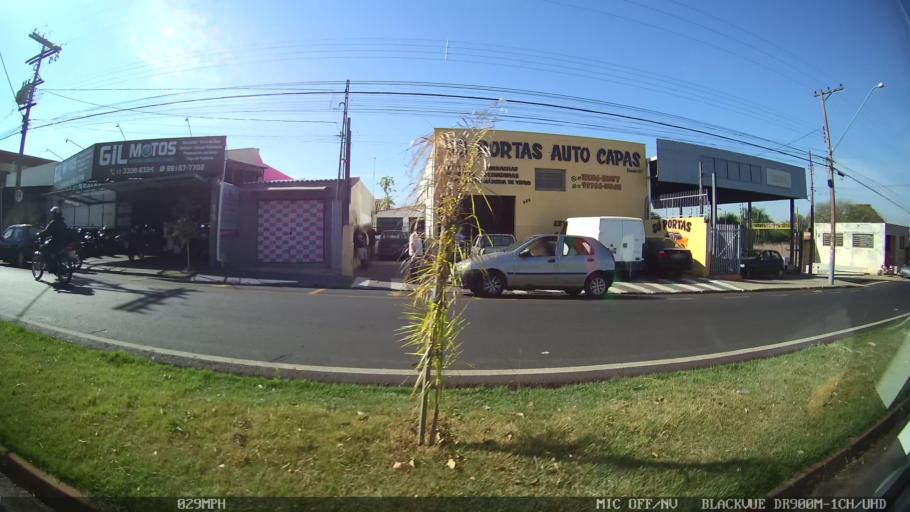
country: BR
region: Sao Paulo
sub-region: Sao Jose Do Rio Preto
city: Sao Jose do Rio Preto
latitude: -20.7869
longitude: -49.3883
